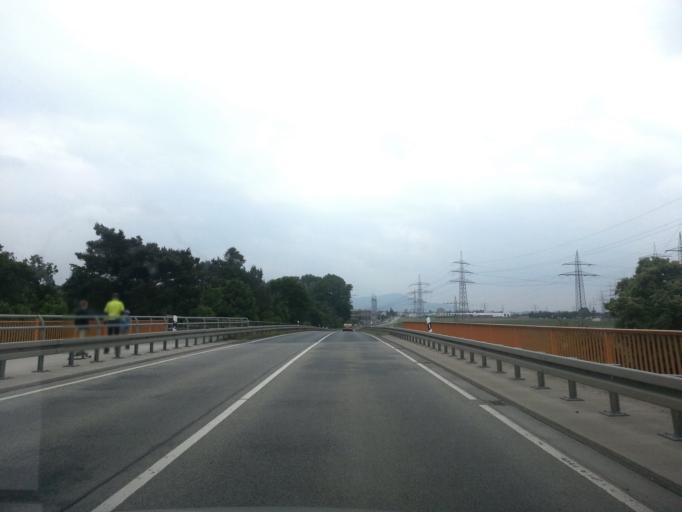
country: DE
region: Hesse
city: Pfungstadt
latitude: 49.8212
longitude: 8.5841
